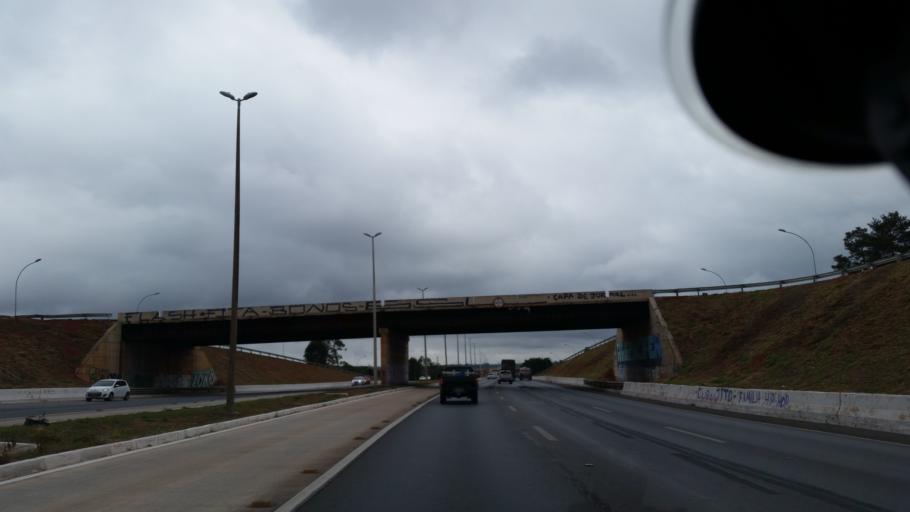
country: BR
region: Federal District
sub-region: Brasilia
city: Brasilia
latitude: -15.9064
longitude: -47.9646
